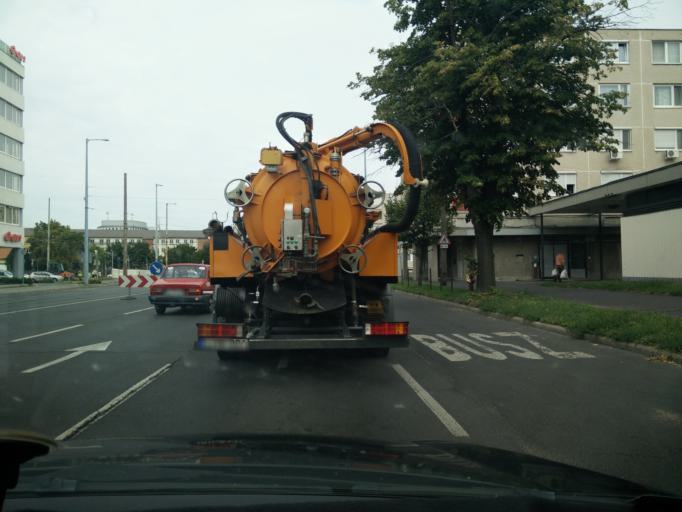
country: HU
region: Hajdu-Bihar
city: Debrecen
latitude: 47.5292
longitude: 21.6317
